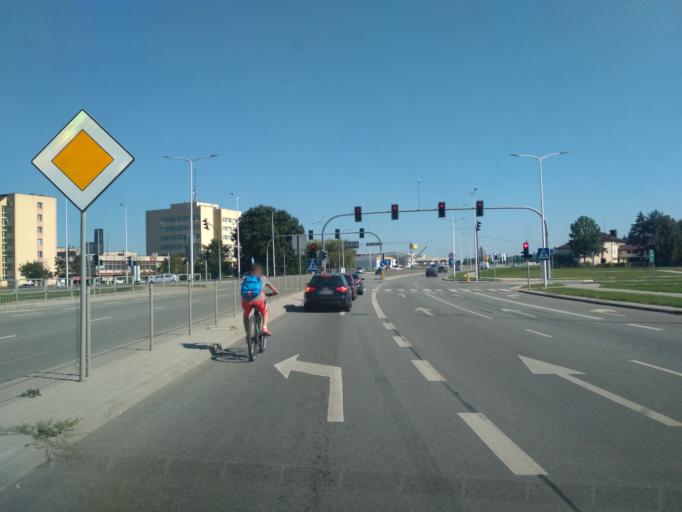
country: PL
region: Subcarpathian Voivodeship
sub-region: Krosno
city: Krosno
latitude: 49.6797
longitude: 21.7717
